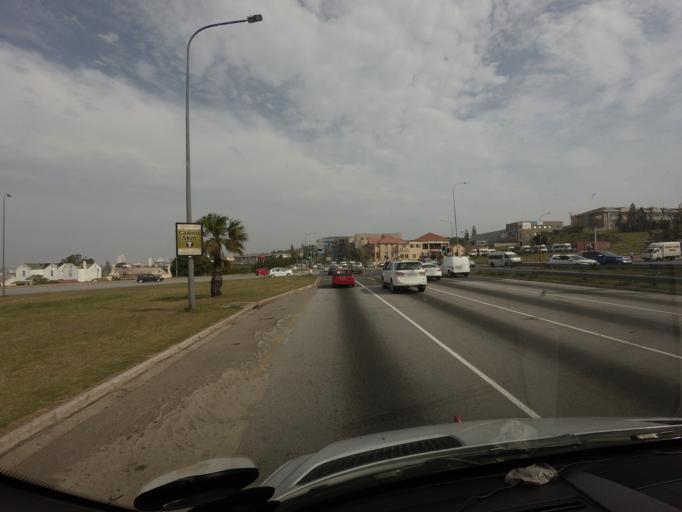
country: ZA
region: Eastern Cape
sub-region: Nelson Mandela Bay Metropolitan Municipality
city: Port Elizabeth
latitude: -33.9683
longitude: 25.6290
